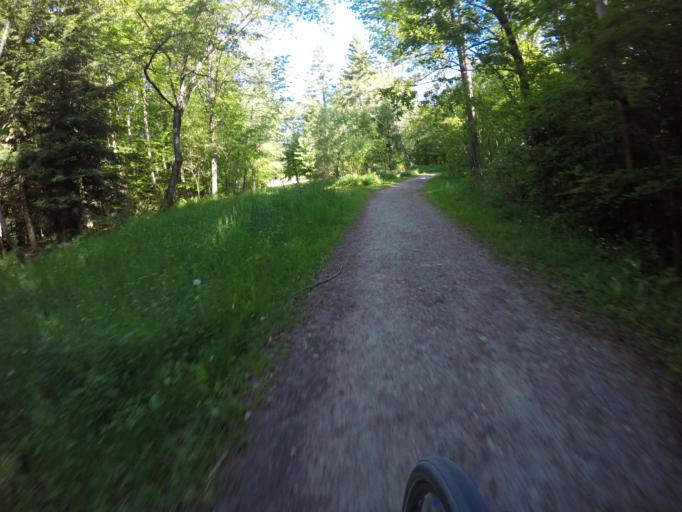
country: DE
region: Baden-Wuerttemberg
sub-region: Regierungsbezirk Stuttgart
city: Gerlingen
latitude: 48.7435
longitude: 9.0625
